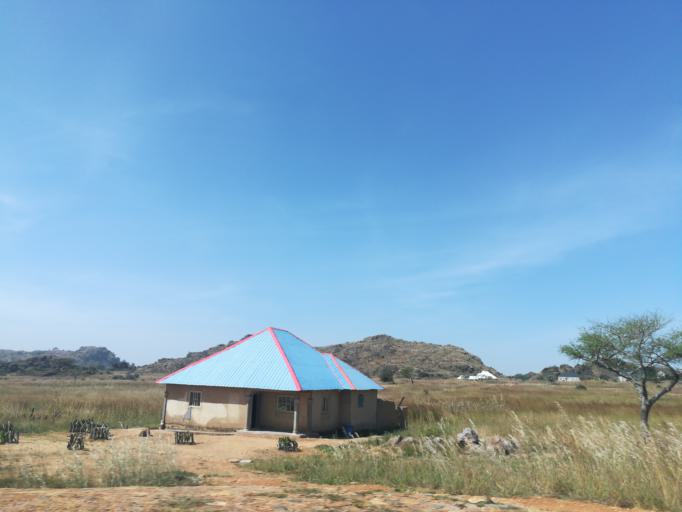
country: NG
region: Plateau
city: Bukuru
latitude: 9.7690
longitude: 8.9014
